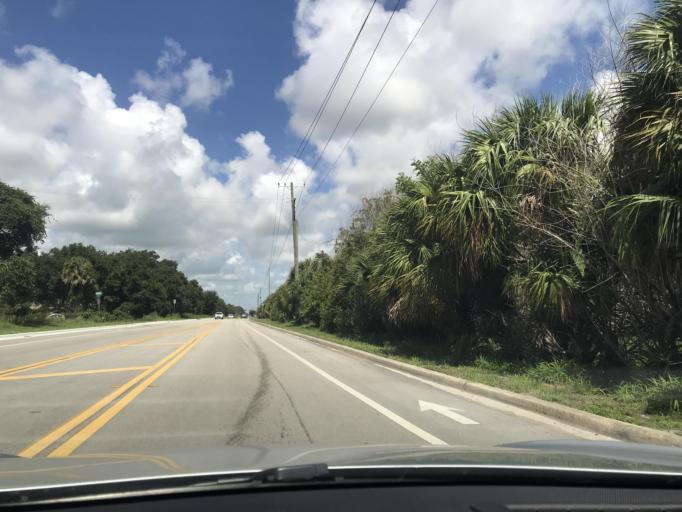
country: US
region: Florida
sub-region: Indian River County
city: Gifford
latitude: 27.6825
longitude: -80.4243
